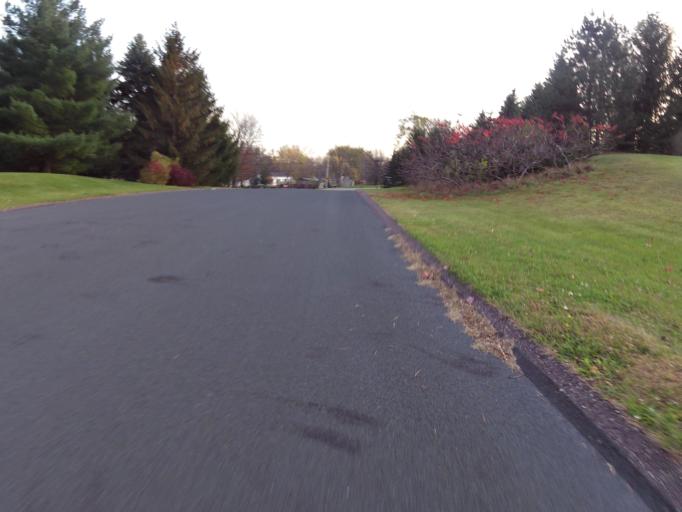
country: US
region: Minnesota
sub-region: Washington County
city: Lake Elmo
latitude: 44.9647
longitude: -92.8745
